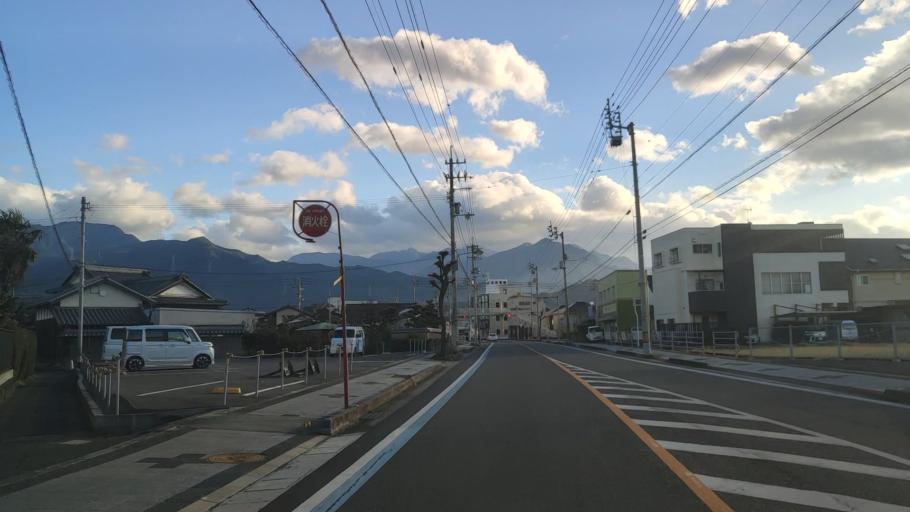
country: JP
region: Ehime
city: Saijo
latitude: 33.9160
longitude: 133.1778
